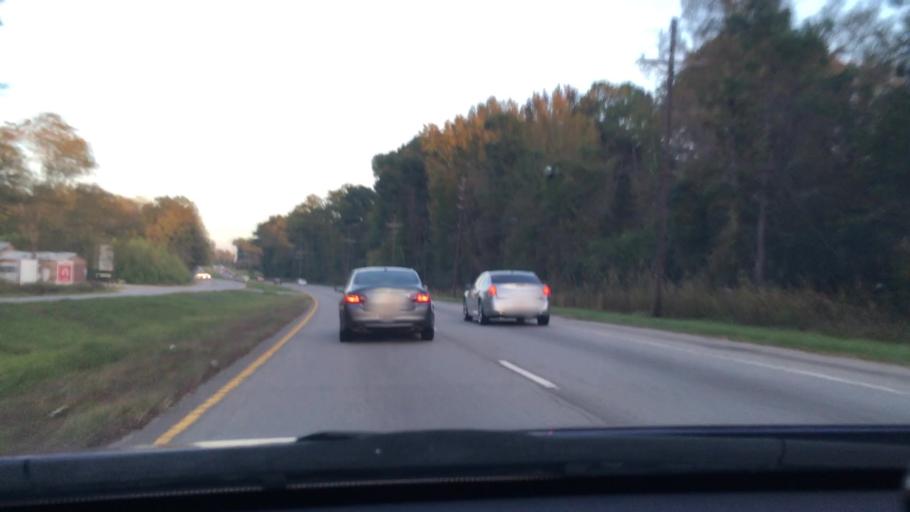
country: US
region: South Carolina
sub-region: Richland County
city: Hopkins
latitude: 33.9438
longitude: -80.9001
